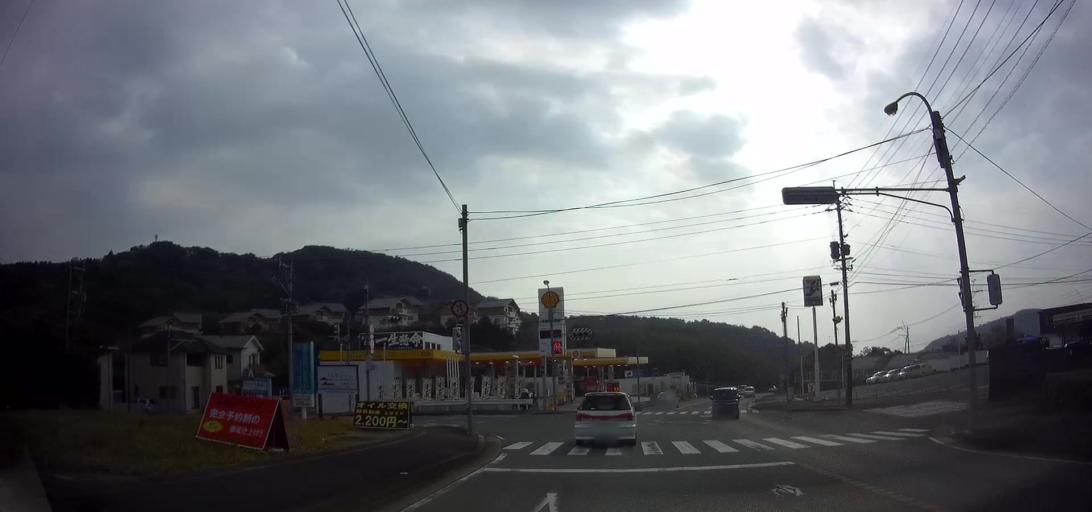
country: JP
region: Nagasaki
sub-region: Isahaya-shi
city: Isahaya
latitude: 32.8008
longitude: 130.1315
